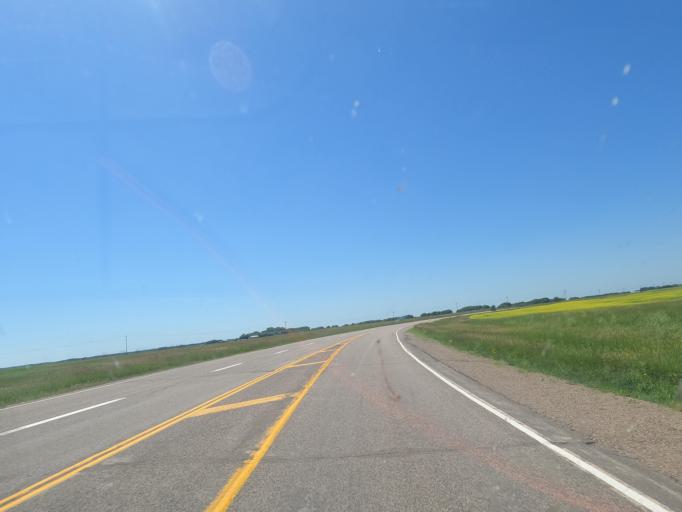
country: CA
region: Manitoba
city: Souris
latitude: 49.5865
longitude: -100.5334
